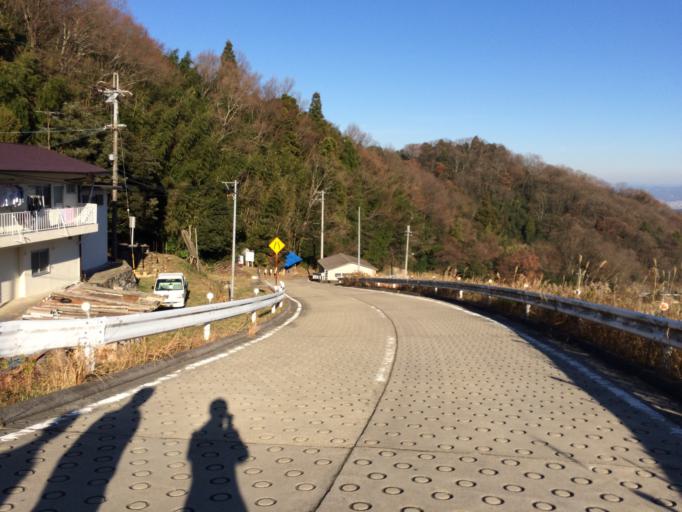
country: JP
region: Nara
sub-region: Ikoma-shi
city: Ikoma
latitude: 34.6661
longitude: 135.6733
